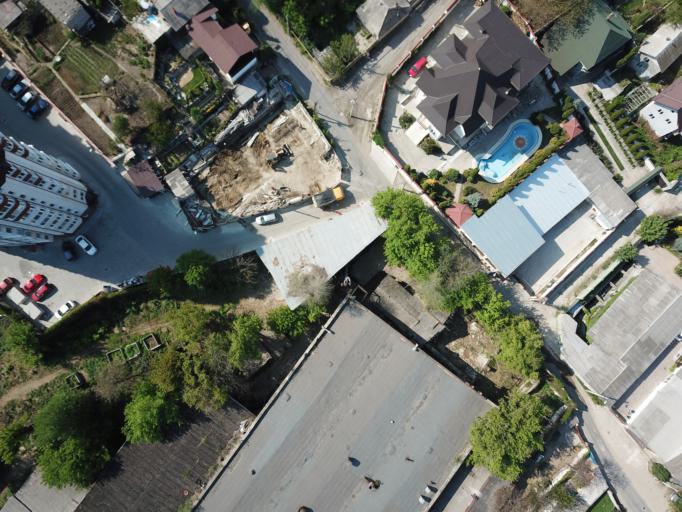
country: MD
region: Chisinau
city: Chisinau
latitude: 47.0110
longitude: 28.8522
